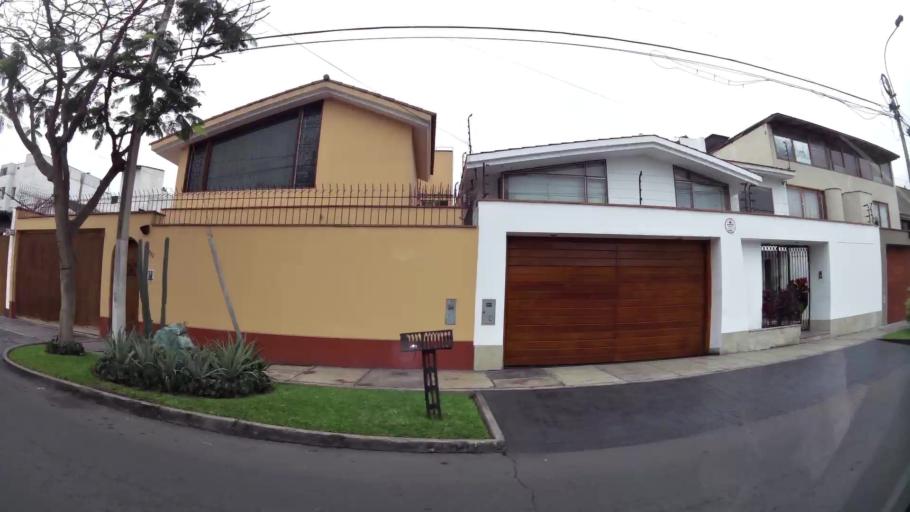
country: PE
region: Lima
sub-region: Lima
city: Surco
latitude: -12.1260
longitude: -77.0062
